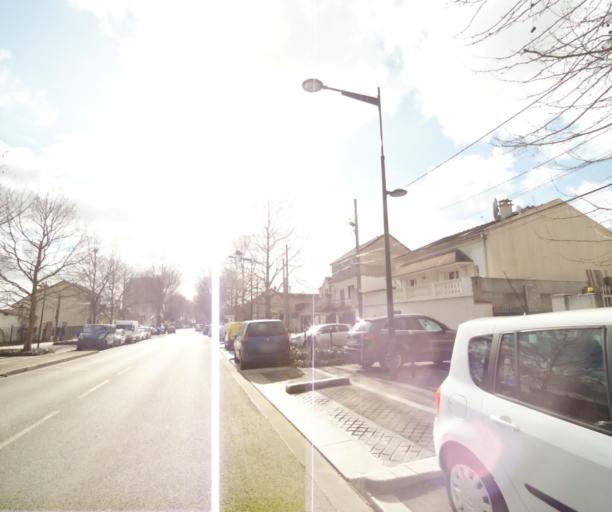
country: FR
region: Ile-de-France
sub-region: Departement de Seine-Saint-Denis
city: Pierrefitte-sur-Seine
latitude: 48.9735
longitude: 2.3655
